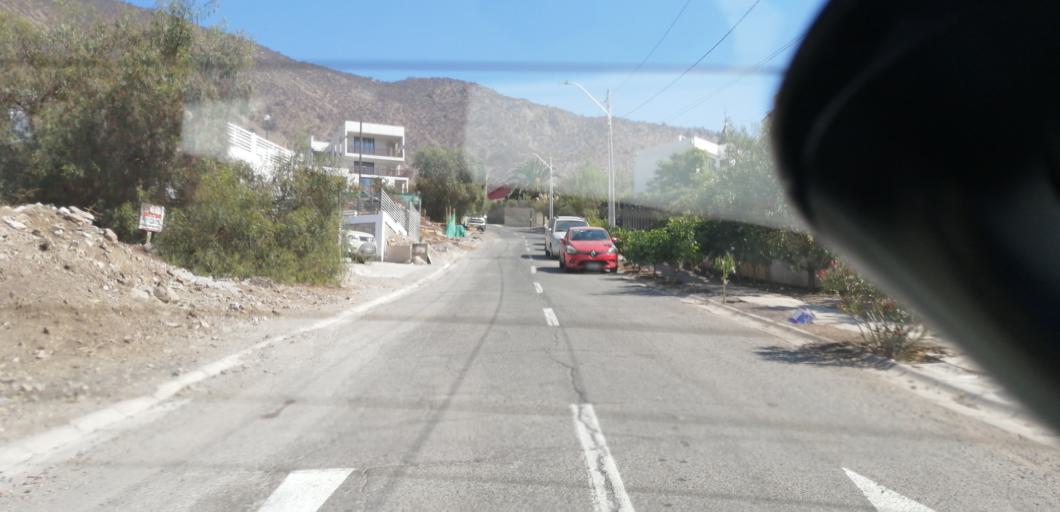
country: CL
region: Santiago Metropolitan
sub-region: Provincia de Santiago
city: Lo Prado
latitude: -33.4594
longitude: -70.8220
